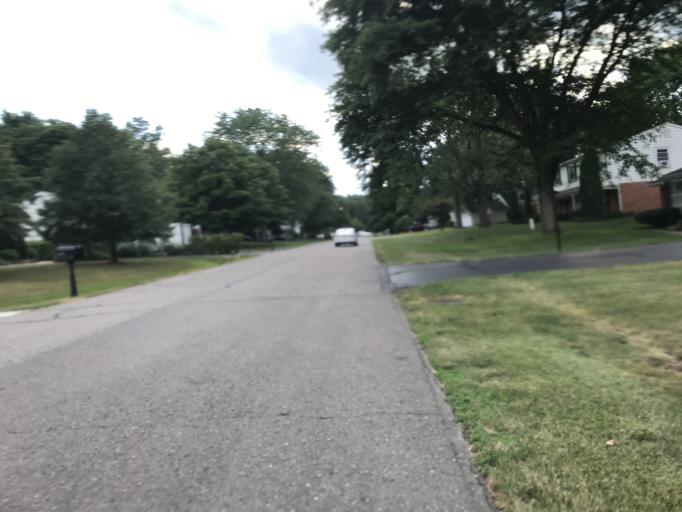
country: US
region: Michigan
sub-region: Oakland County
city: Farmington Hills
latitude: 42.4861
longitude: -83.3437
